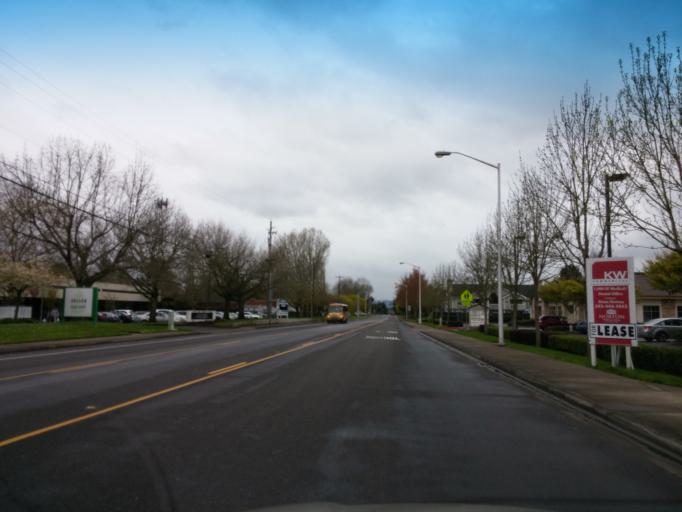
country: US
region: Oregon
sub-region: Washington County
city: Oak Hills
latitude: 45.5332
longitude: -122.8547
